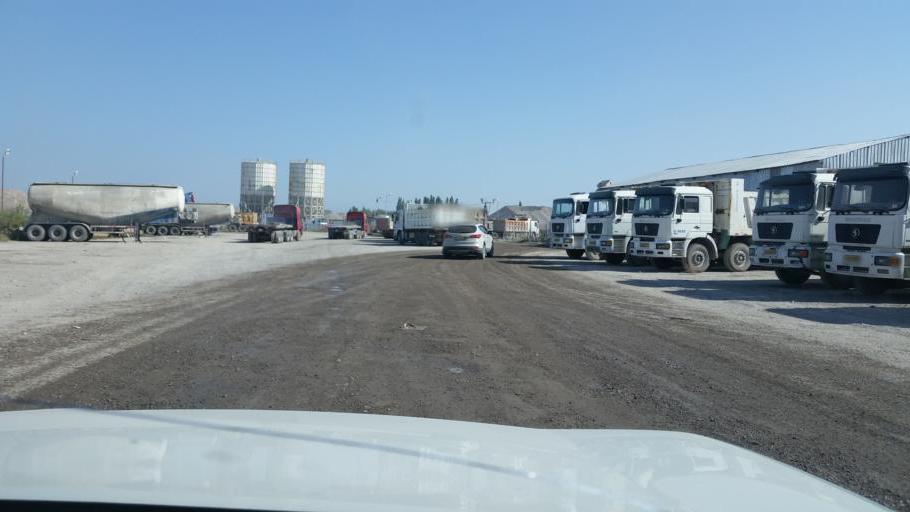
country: KZ
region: Almaty Oblysy
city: Turgen'
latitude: 43.5246
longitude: 77.5644
